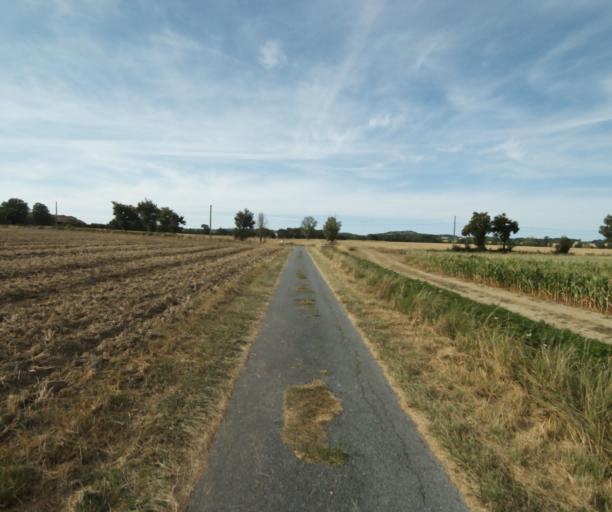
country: FR
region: Midi-Pyrenees
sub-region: Departement du Tarn
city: Puylaurens
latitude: 43.5235
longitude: 2.0288
